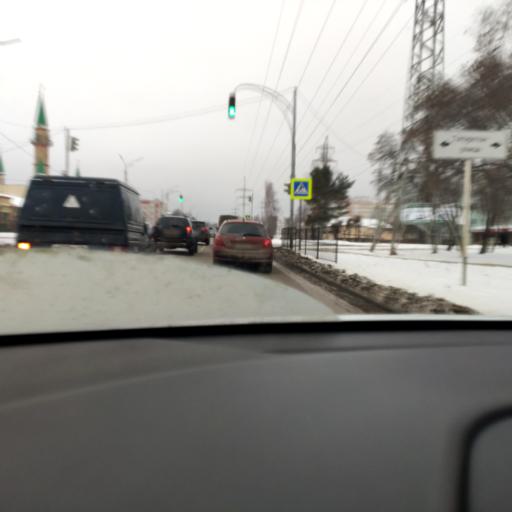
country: RU
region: Tatarstan
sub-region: Zelenodol'skiy Rayon
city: Zelenodolsk
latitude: 55.8532
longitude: 48.5033
